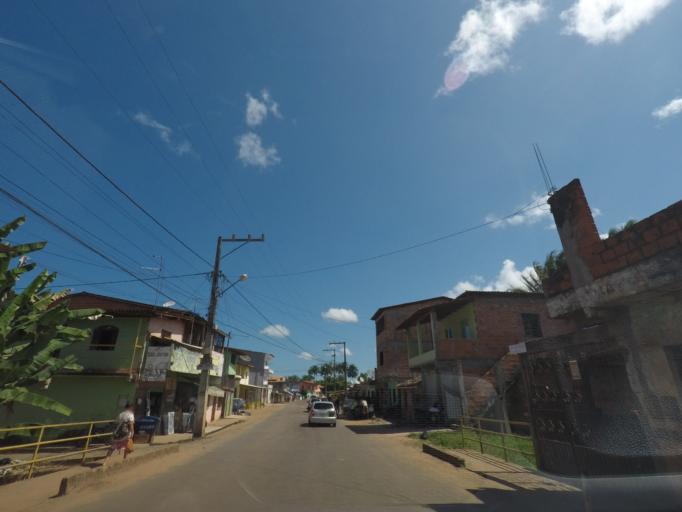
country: BR
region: Bahia
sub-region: Taperoa
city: Taperoa
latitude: -13.5447
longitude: -39.0993
